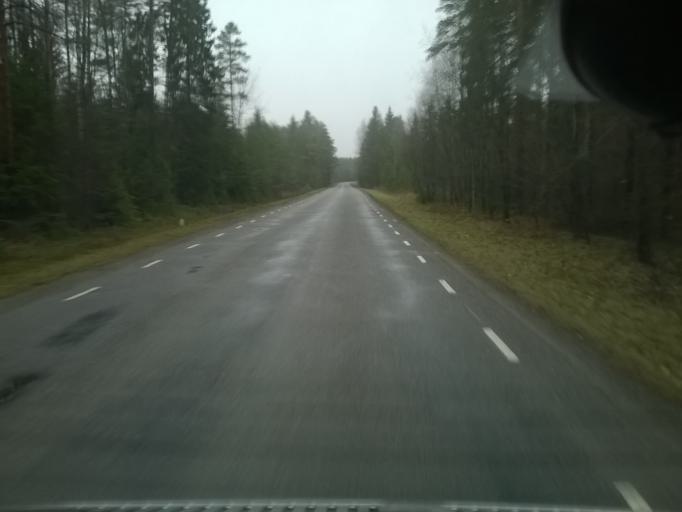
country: EE
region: Raplamaa
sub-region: Kohila vald
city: Kohila
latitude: 59.1906
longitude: 24.6621
